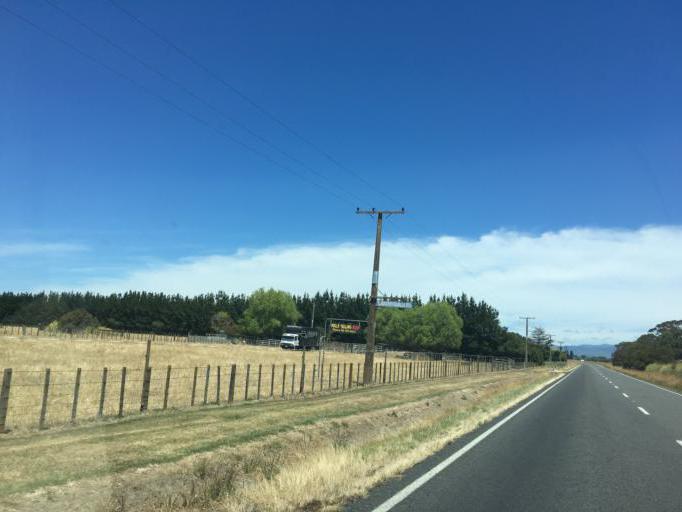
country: NZ
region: Hawke's Bay
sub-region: Hastings District
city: Hastings
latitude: -39.9965
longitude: 176.4226
